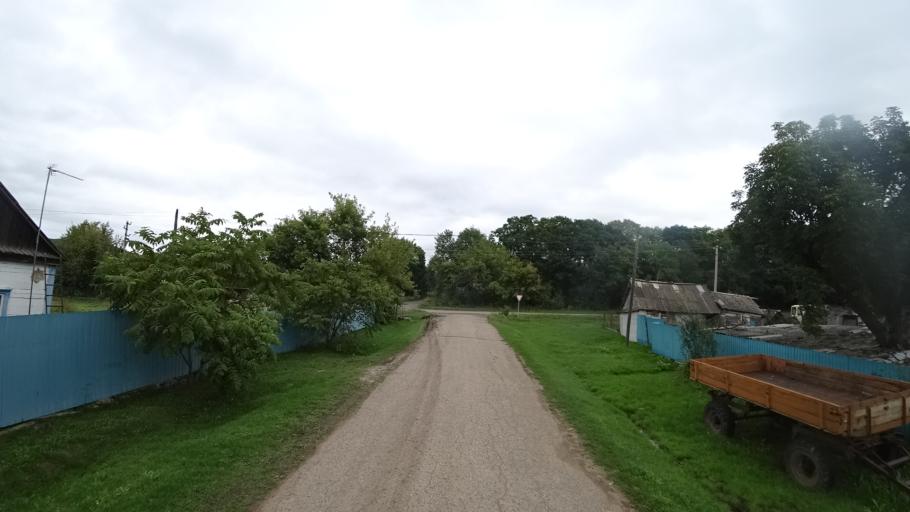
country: RU
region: Primorskiy
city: Chernigovka
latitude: 44.4560
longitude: 132.5931
